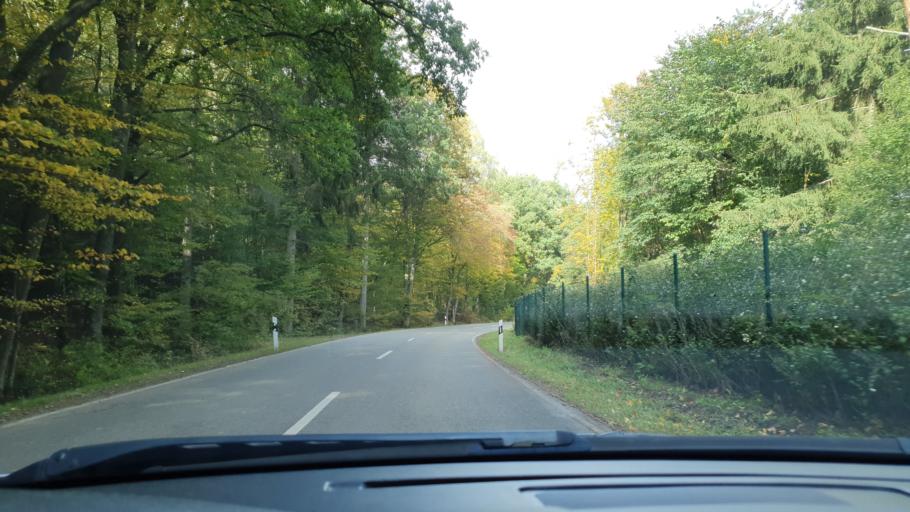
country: DE
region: Rheinland-Pfalz
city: Kaiserslautern
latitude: 49.4261
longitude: 7.8176
